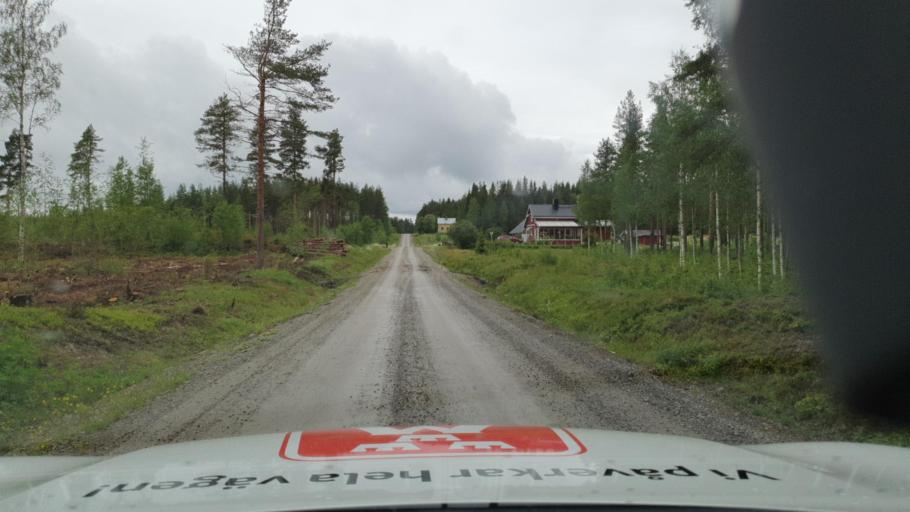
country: SE
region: Vaesterbotten
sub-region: Dorotea Kommun
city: Dorotea
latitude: 64.0665
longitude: 16.7042
